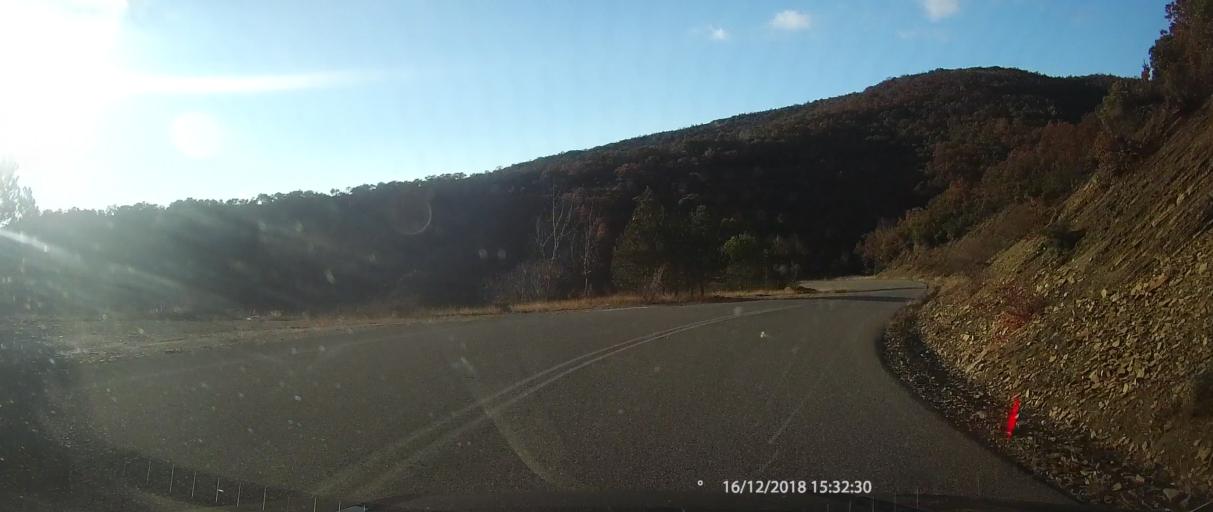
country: GR
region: Epirus
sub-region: Nomos Ioanninon
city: Konitsa
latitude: 40.0690
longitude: 20.7401
